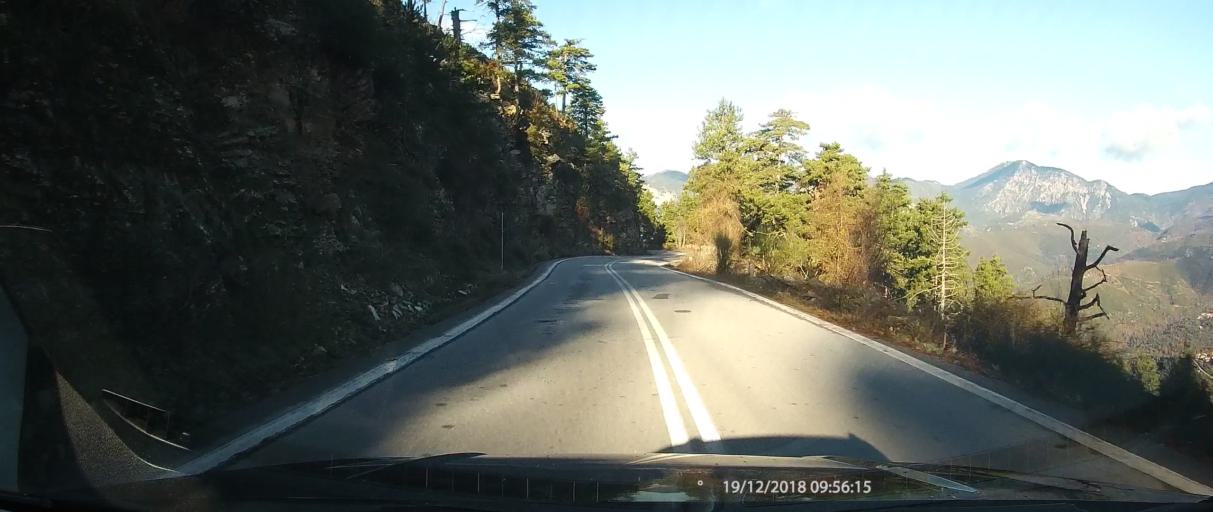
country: GR
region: Peloponnese
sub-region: Nomos Messinias
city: Paralia Vergas
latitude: 37.0850
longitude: 22.2410
